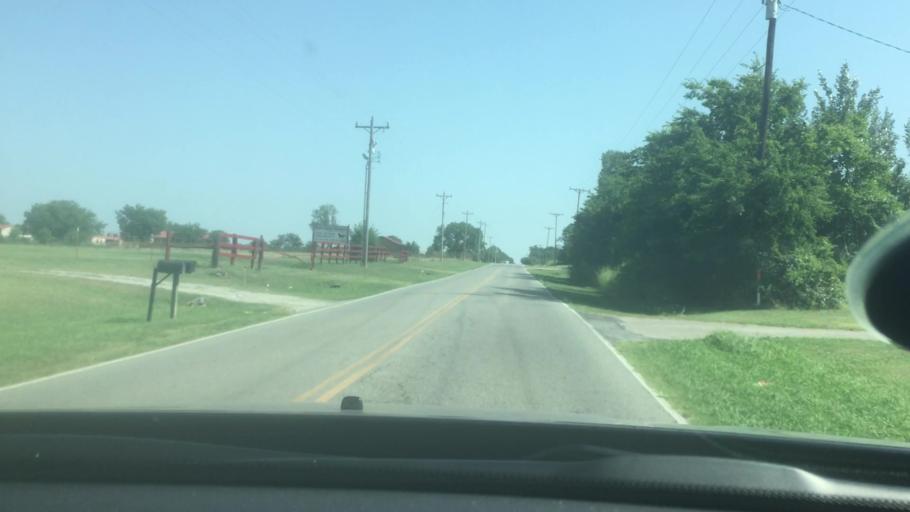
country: US
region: Oklahoma
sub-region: Bryan County
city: Calera
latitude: 34.0043
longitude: -96.4656
